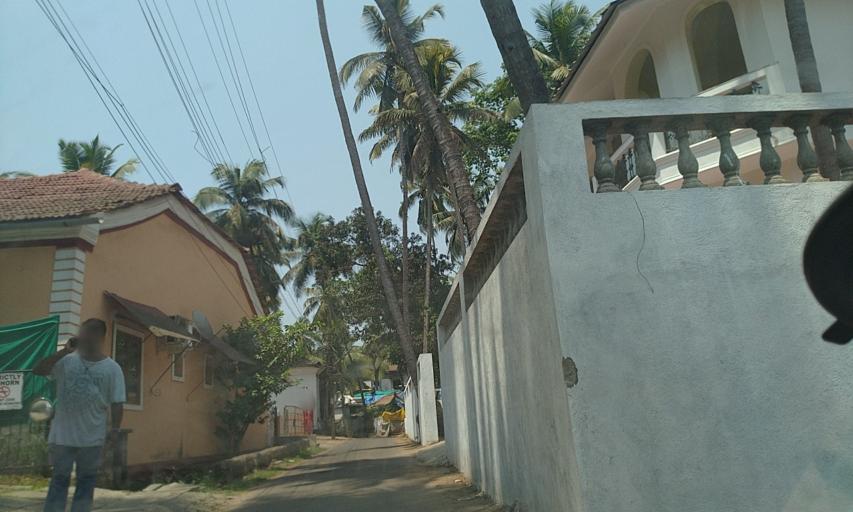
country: IN
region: Goa
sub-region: North Goa
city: Saligao
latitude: 15.5491
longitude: 73.7860
